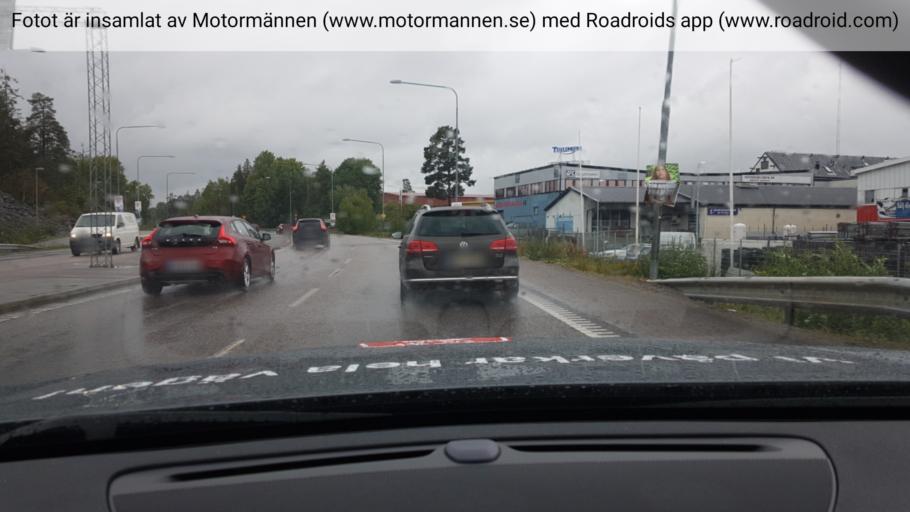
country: SE
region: Stockholm
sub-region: Haninge Kommun
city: Handen
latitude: 59.2000
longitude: 18.1270
